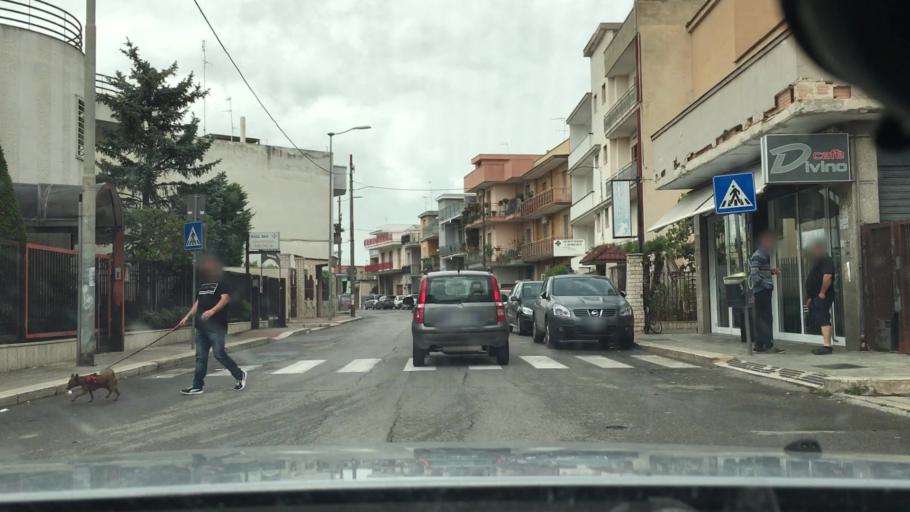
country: IT
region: Apulia
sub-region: Provincia di Bari
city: Capurso
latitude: 41.0467
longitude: 16.9278
